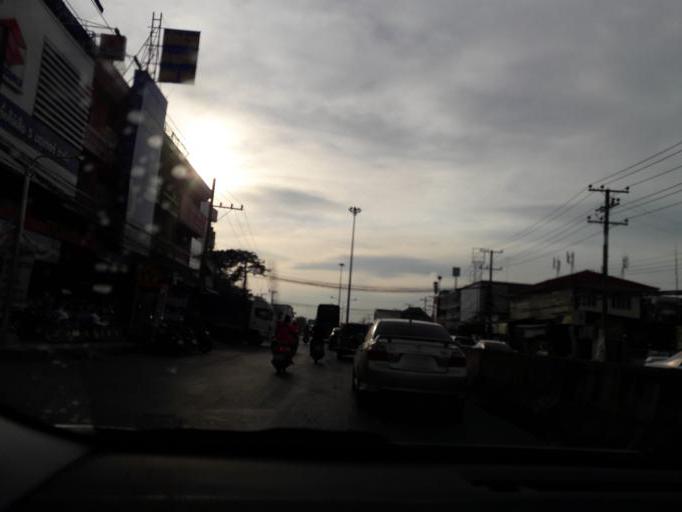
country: TH
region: Ang Thong
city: Ang Thong
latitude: 14.5935
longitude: 100.4493
